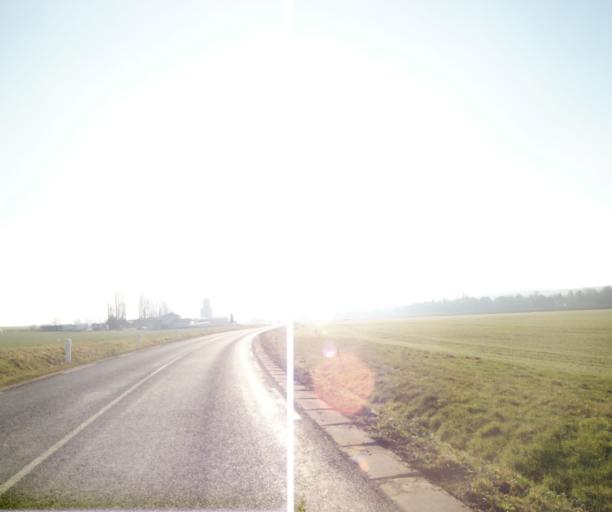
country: FR
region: Champagne-Ardenne
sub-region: Departement de la Haute-Marne
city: Wassy
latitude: 48.5165
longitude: 4.9358
